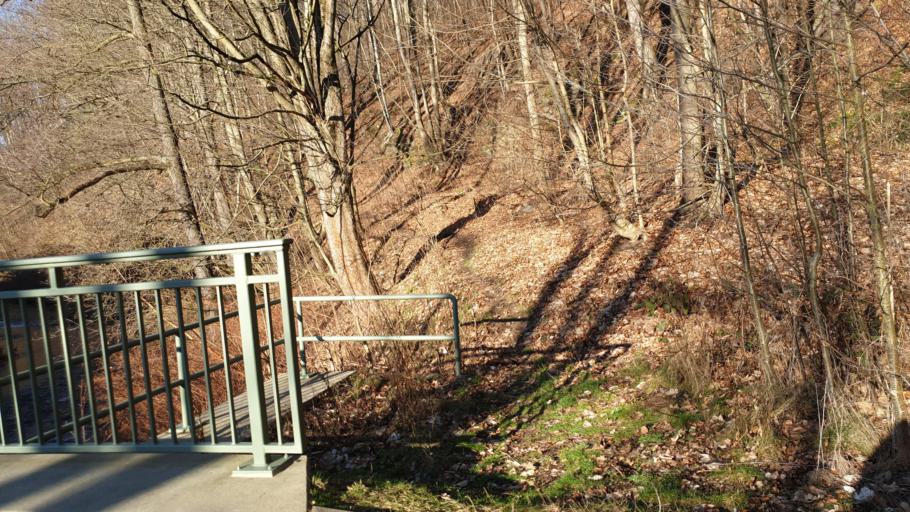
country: DE
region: Saxony
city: Gelenau
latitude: 50.7636
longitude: 12.9792
